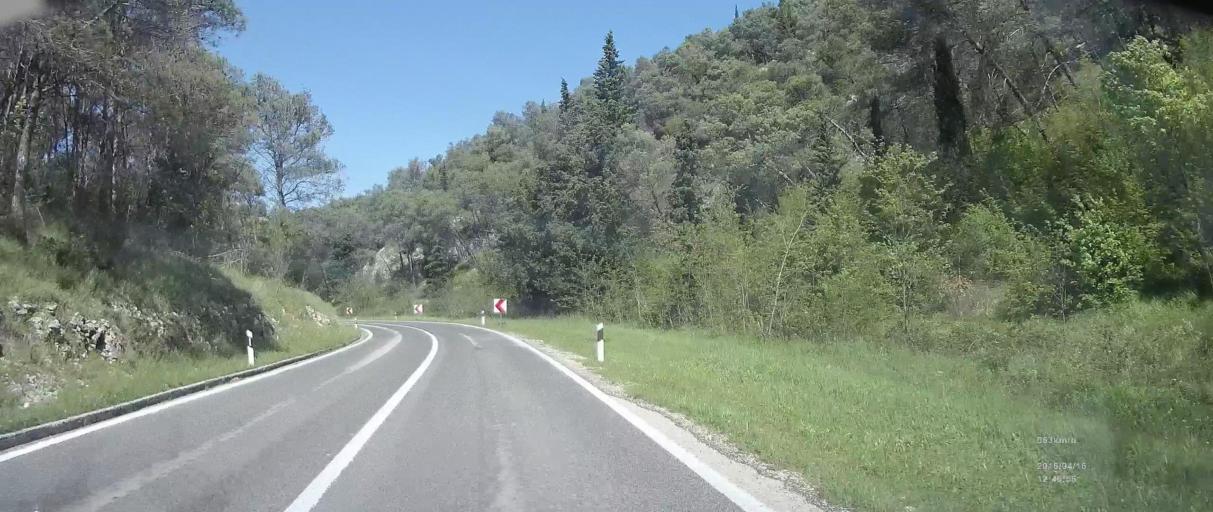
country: HR
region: Sibensko-Kniniska
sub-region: Grad Sibenik
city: Brodarica
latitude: 43.6591
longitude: 16.0506
